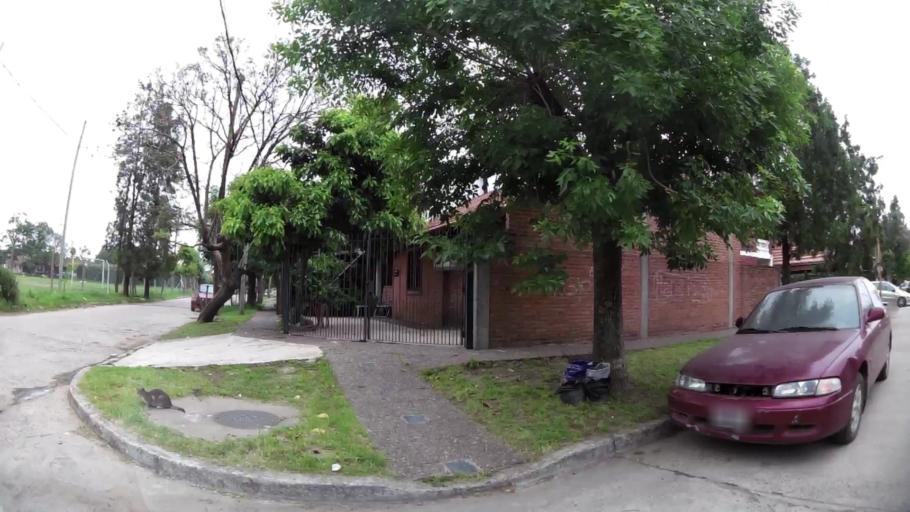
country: AR
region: Buenos Aires
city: San Justo
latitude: -34.7123
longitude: -58.5354
